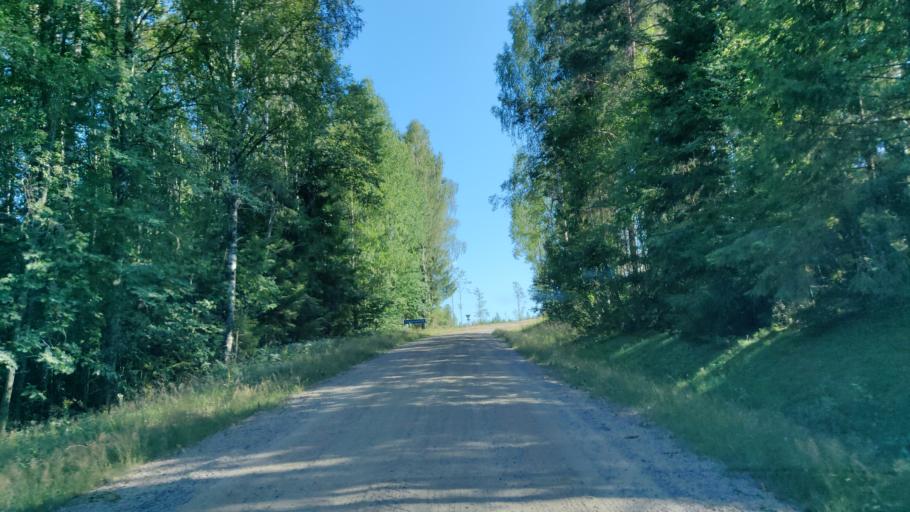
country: SE
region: Vaermland
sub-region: Hagfors Kommun
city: Ekshaerad
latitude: 60.1541
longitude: 13.5165
